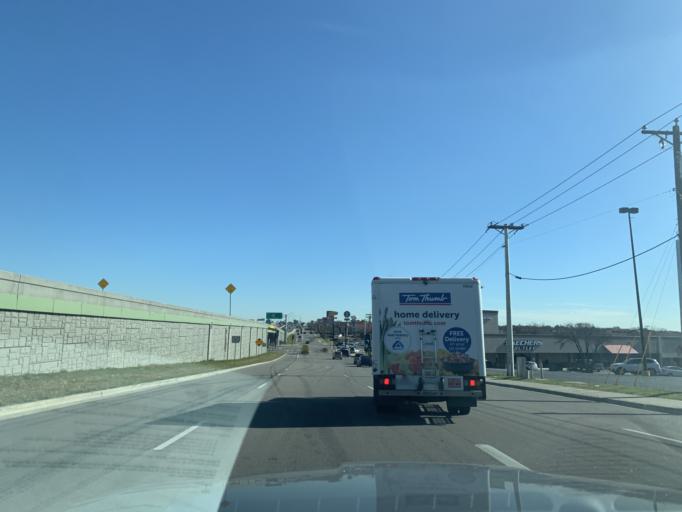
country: US
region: Texas
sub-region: Tarrant County
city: Euless
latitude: 32.8372
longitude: -97.1017
